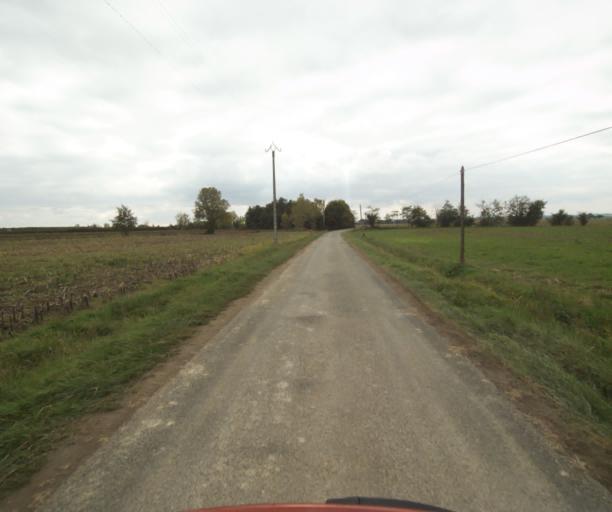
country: FR
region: Midi-Pyrenees
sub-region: Departement du Tarn-et-Garonne
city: Verdun-sur-Garonne
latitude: 43.8904
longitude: 1.2640
